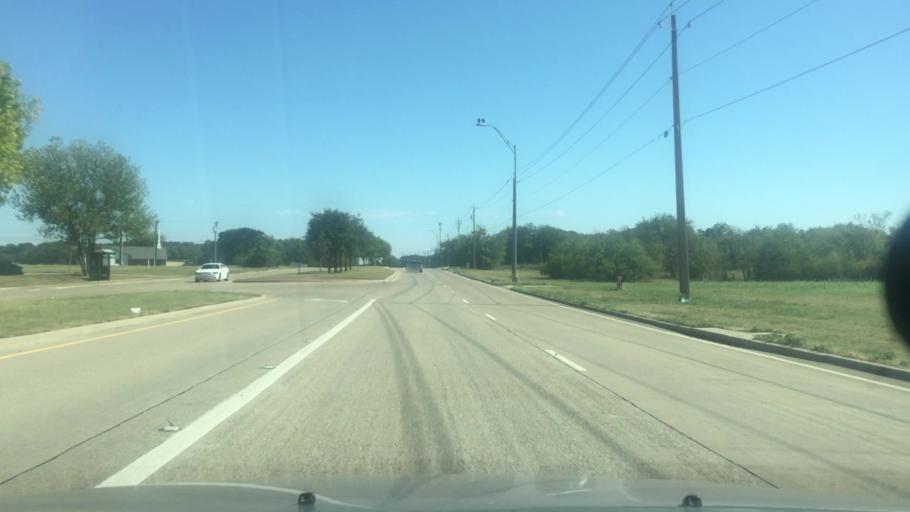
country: US
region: Texas
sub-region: Denton County
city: Denton
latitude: 33.2447
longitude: -97.1413
